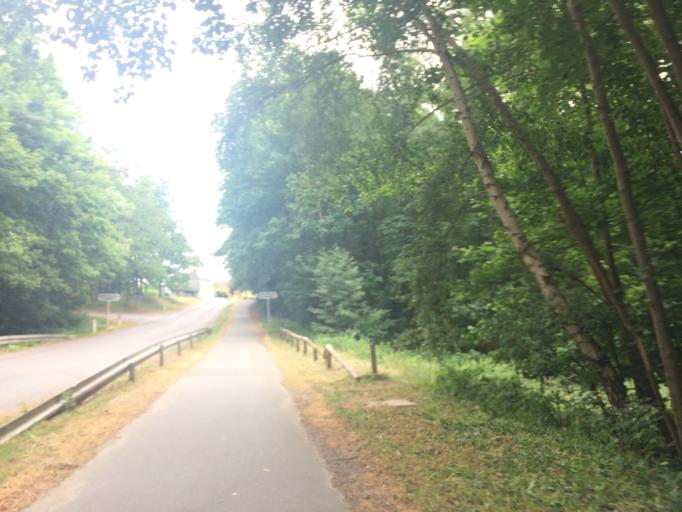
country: DK
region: Capital Region
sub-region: Bornholm Kommune
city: Ronne
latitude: 55.1559
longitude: 14.7157
